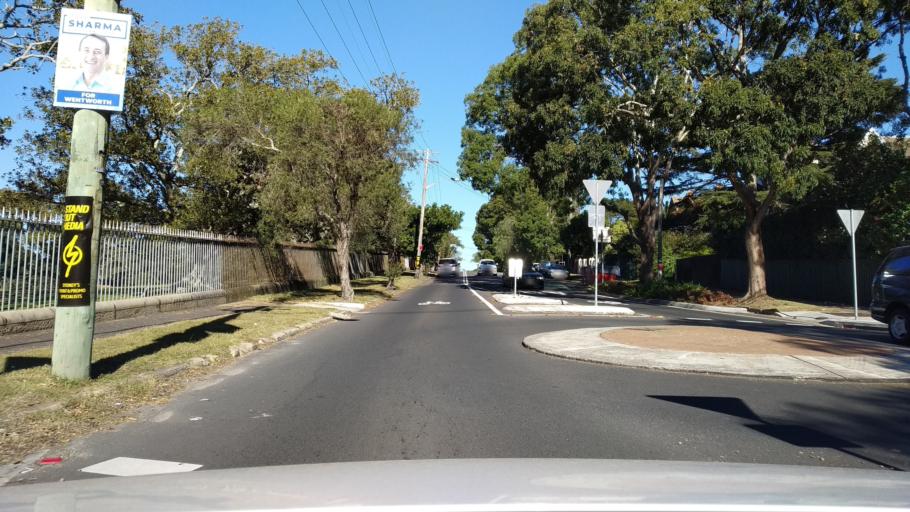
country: AU
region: New South Wales
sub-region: Woollahra
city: Woollahra
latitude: -33.8948
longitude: 151.2306
